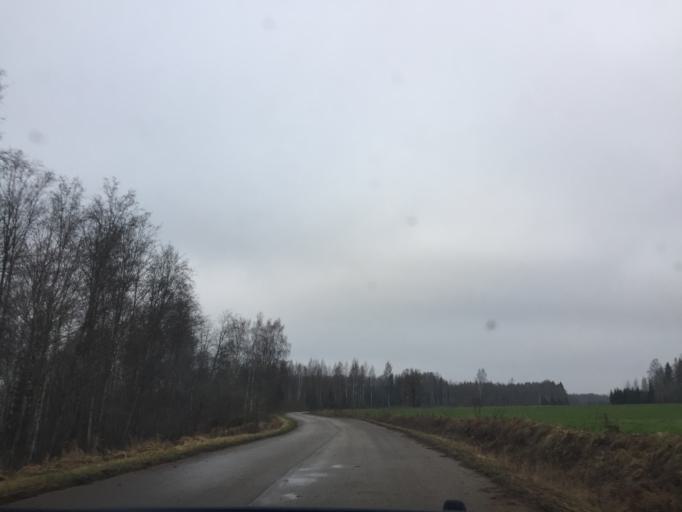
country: LV
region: Koceni
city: Koceni
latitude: 57.5158
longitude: 25.1787
